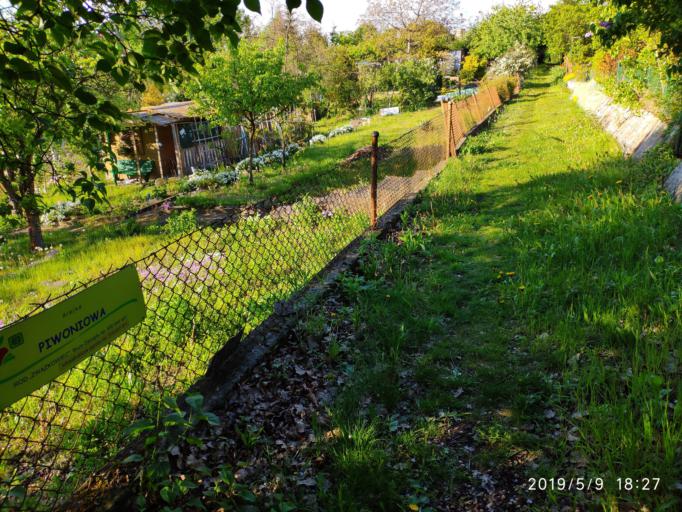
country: PL
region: Lubusz
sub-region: Zielona Gora
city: Zielona Gora
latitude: 51.9288
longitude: 15.5232
